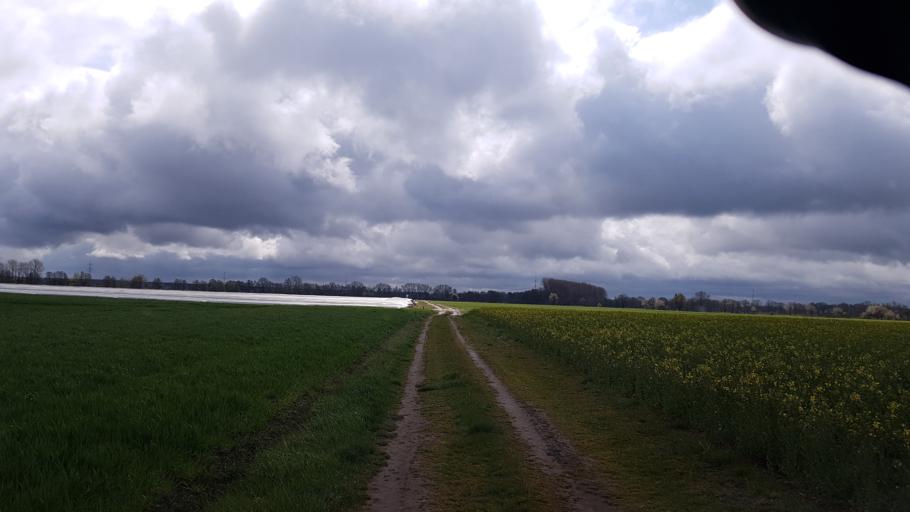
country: DE
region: Brandenburg
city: Doberlug-Kirchhain
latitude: 51.6581
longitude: 13.5520
